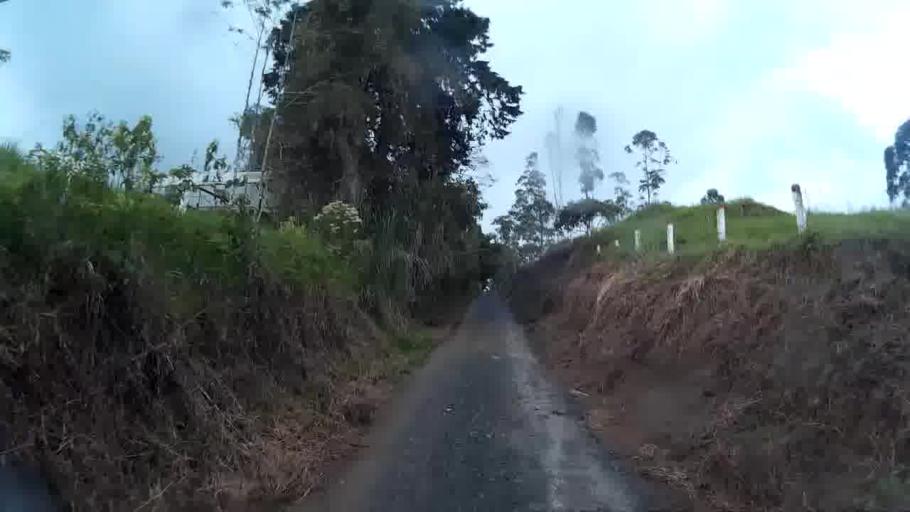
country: CO
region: Quindio
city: Filandia
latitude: 4.6881
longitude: -75.6623
